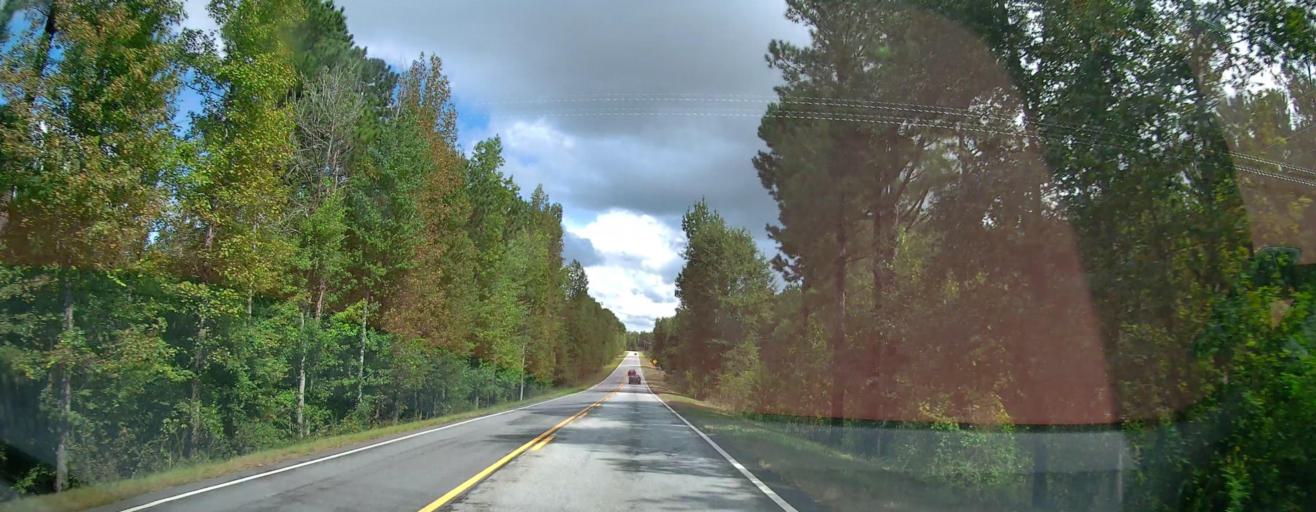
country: US
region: Georgia
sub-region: Jones County
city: Gray
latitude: 32.9597
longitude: -83.4396
